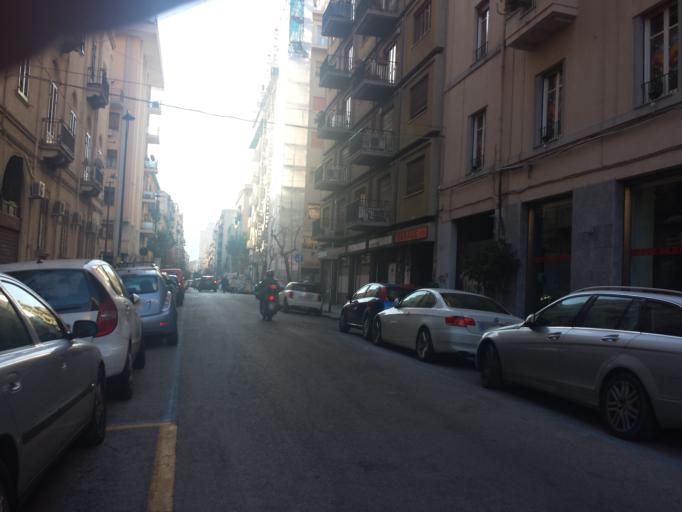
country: IT
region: Sicily
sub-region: Palermo
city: Palermo
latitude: 38.1284
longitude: 13.3509
